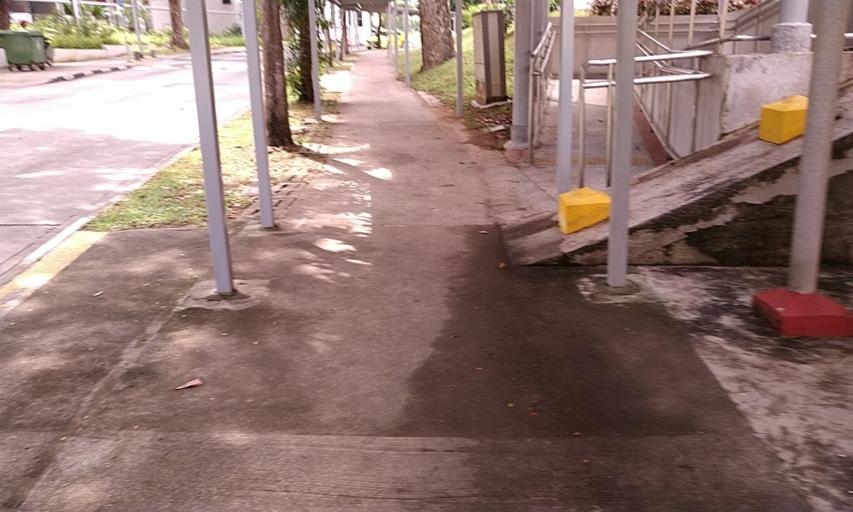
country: SG
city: Singapore
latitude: 1.2894
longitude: 103.8139
